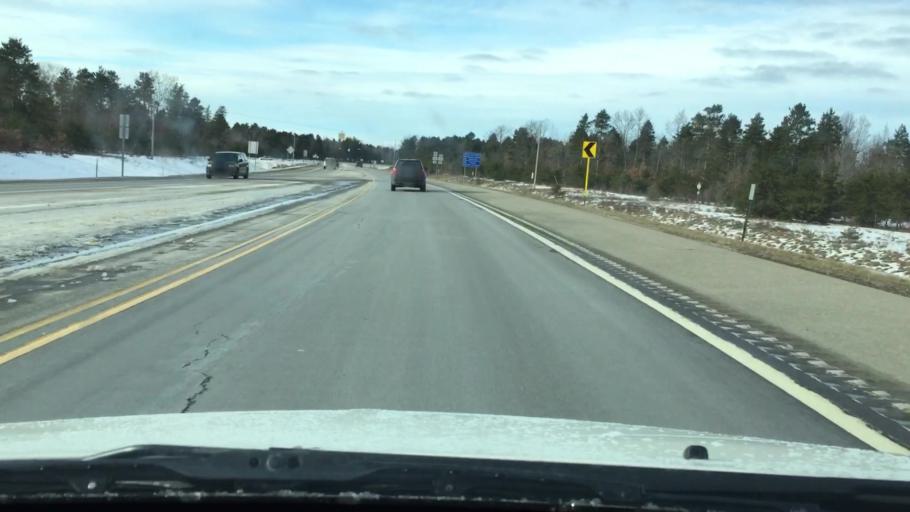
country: US
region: Michigan
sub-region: Wexford County
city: Manton
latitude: 44.4663
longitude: -85.3982
